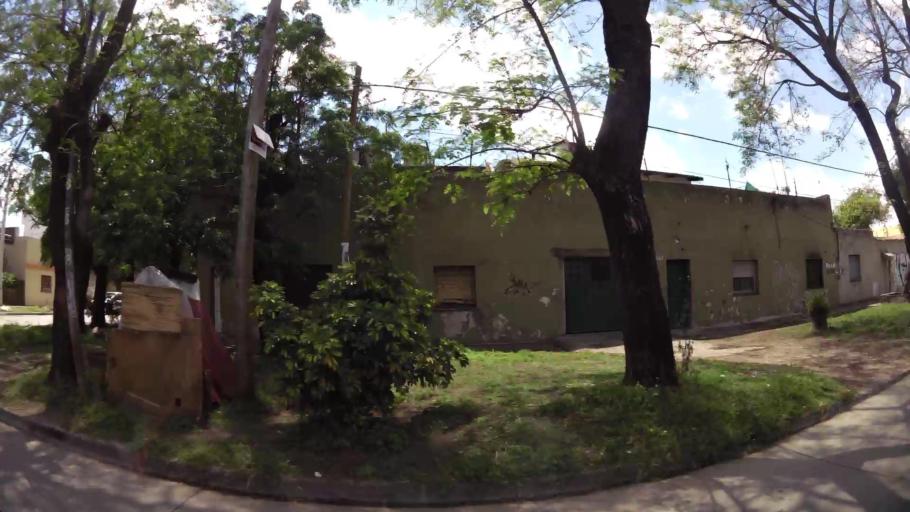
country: AR
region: Buenos Aires F.D.
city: Villa Lugano
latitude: -34.6894
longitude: -58.4370
